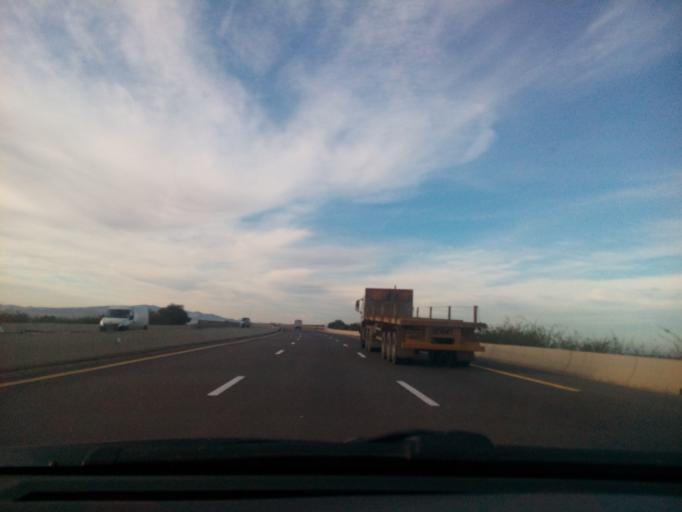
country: DZ
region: Mascara
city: Mascara
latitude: 35.6497
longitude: 0.1029
